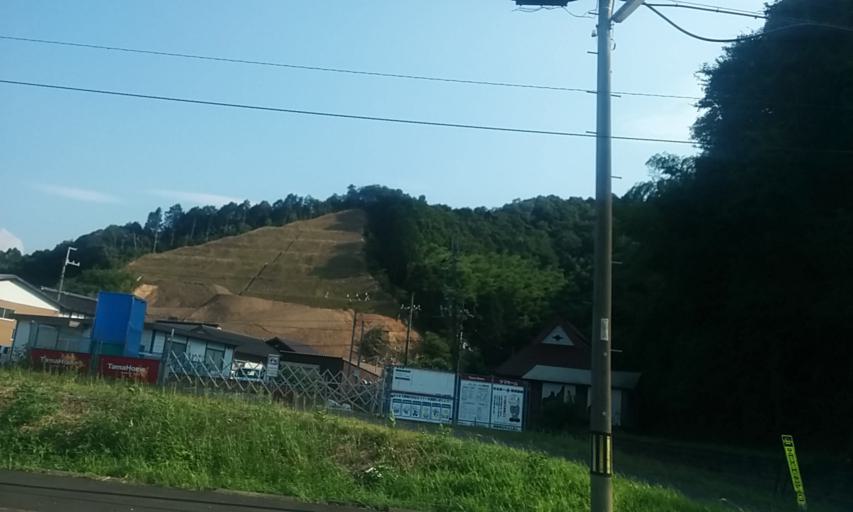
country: JP
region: Kyoto
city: Maizuru
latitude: 35.4543
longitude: 135.2761
